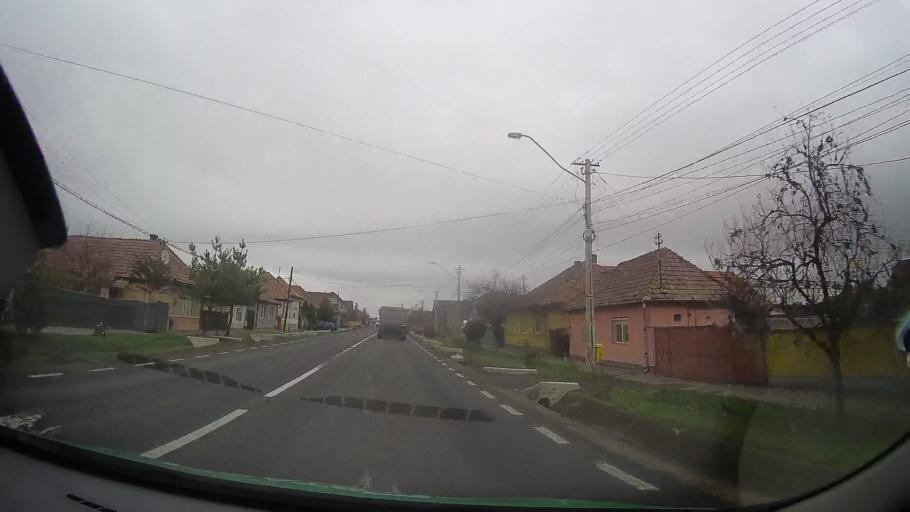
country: RO
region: Mures
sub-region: Municipiul Reghin
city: Reghin
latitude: 46.7716
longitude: 24.6880
